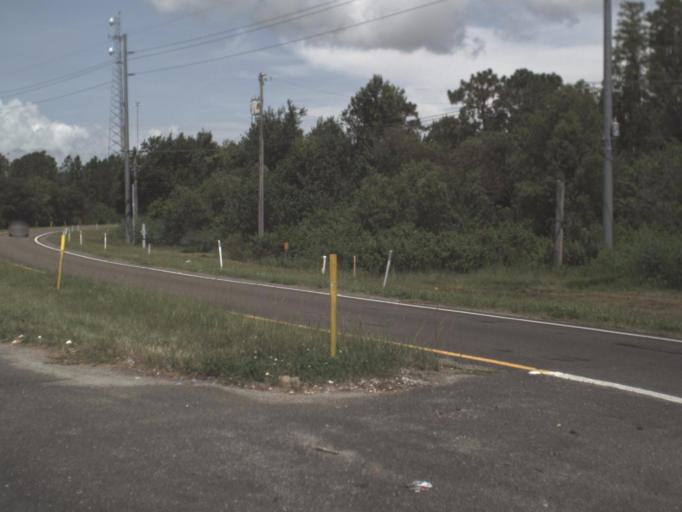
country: US
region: Florida
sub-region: Hillsborough County
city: Sun City Center
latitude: 27.7126
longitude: -82.3796
